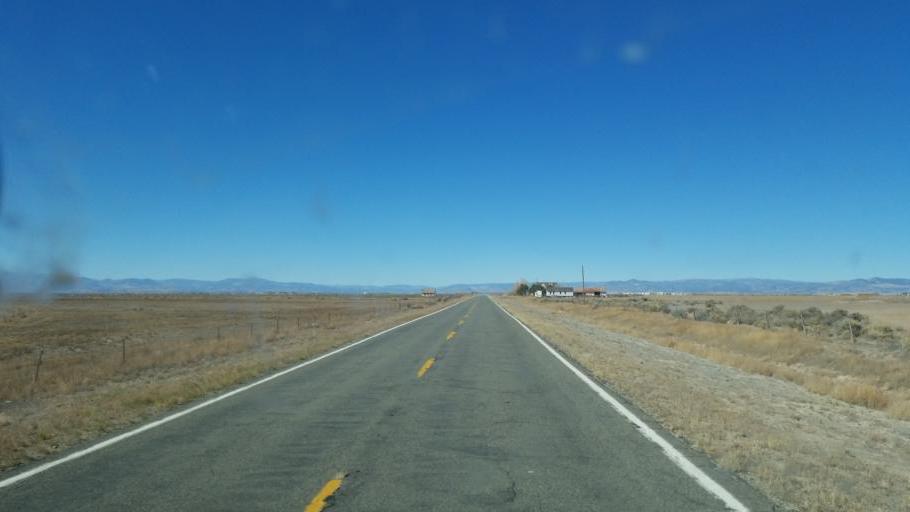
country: US
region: Colorado
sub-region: Saguache County
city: Center
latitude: 37.7488
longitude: -105.9525
